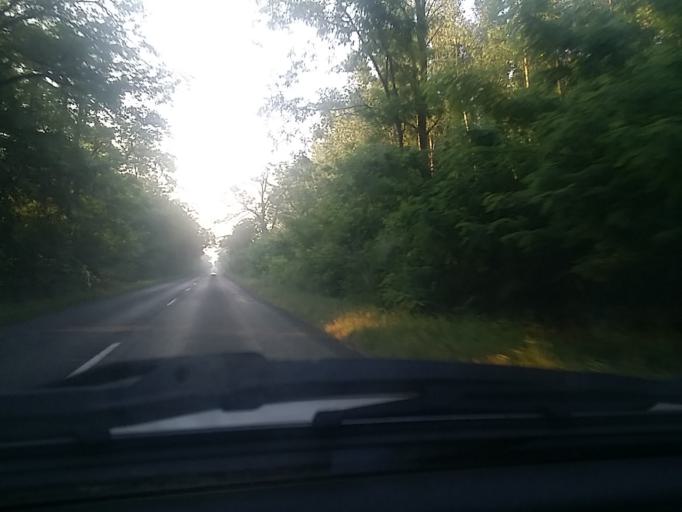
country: HU
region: Pest
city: Forropuszta
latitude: 47.4631
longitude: 19.6527
